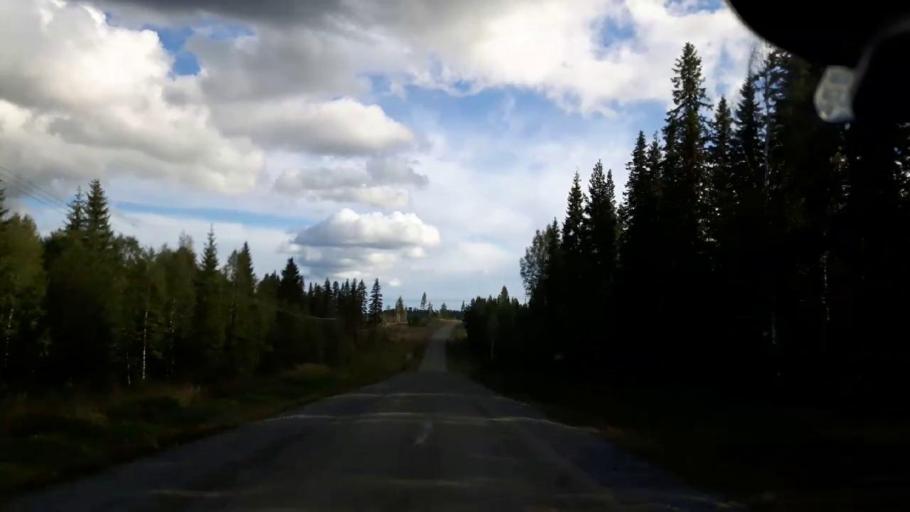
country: SE
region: Jaemtland
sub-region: Stroemsunds Kommun
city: Stroemsund
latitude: 63.3131
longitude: 15.5897
